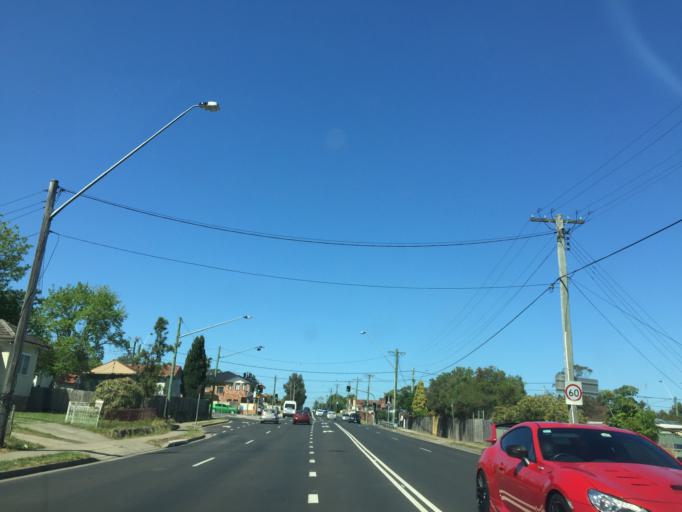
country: AU
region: New South Wales
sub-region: Blacktown
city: Blacktown
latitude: -33.7721
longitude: 150.9032
